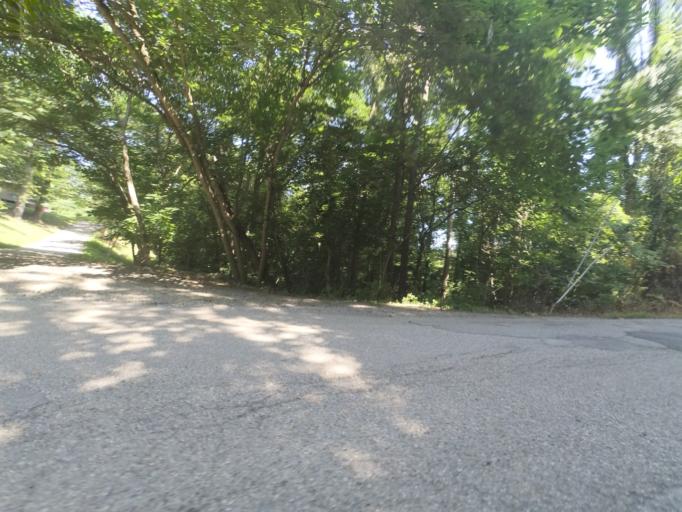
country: US
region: West Virginia
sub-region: Cabell County
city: Huntington
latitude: 38.4327
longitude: -82.4489
